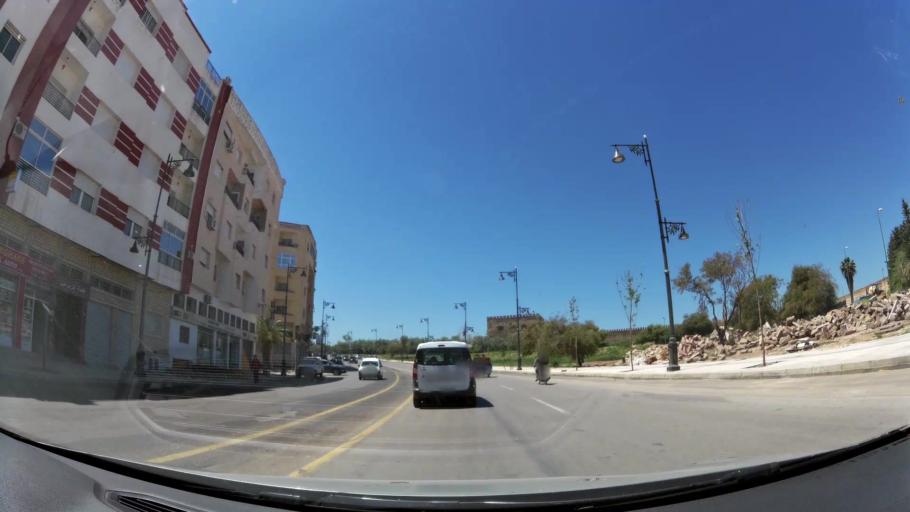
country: MA
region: Meknes-Tafilalet
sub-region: Meknes
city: Meknes
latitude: 33.8707
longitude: -5.5384
